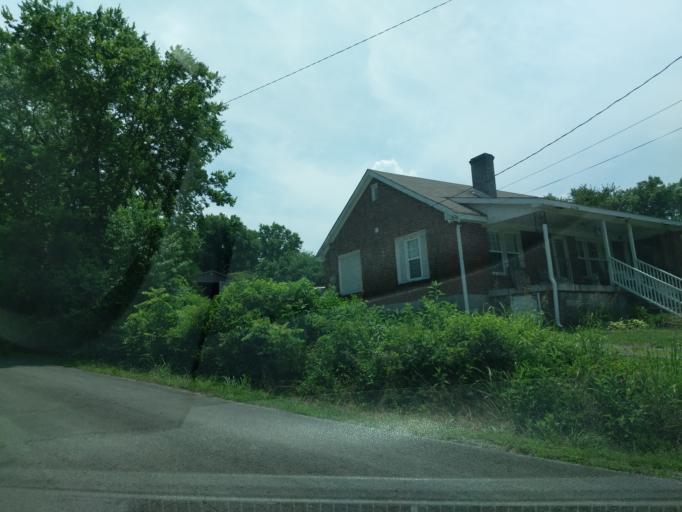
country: US
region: Tennessee
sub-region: Davidson County
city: Lakewood
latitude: 36.2267
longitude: -86.6295
